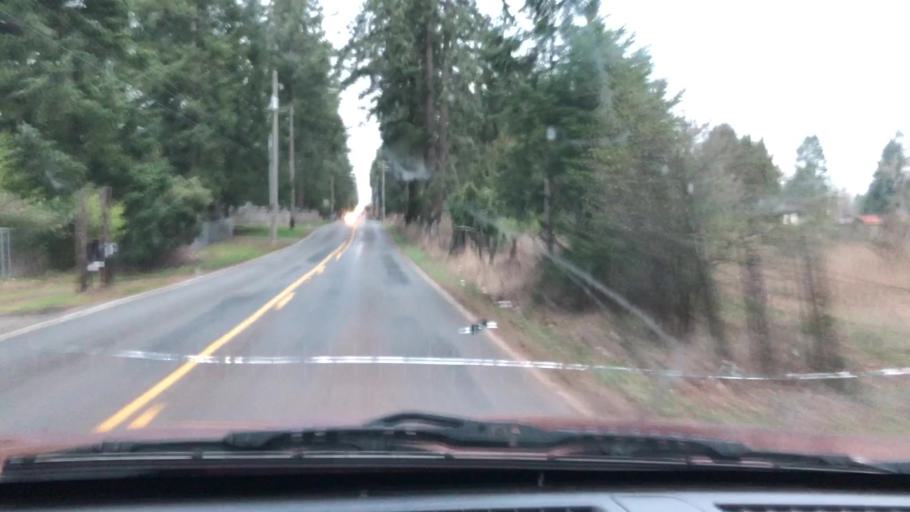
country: US
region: Washington
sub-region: Pierce County
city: Elk Plain
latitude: 47.0625
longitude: -122.4003
